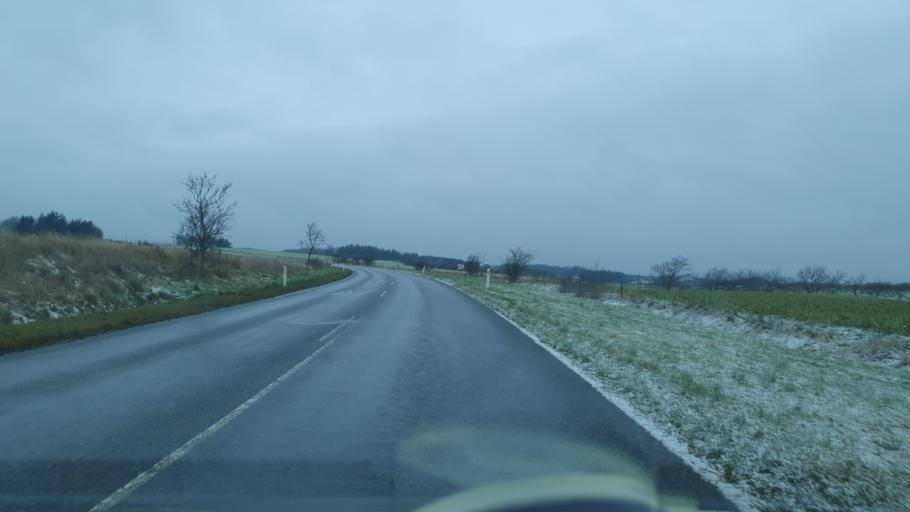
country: DK
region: North Denmark
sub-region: Jammerbugt Kommune
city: Brovst
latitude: 57.1241
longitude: 9.4896
